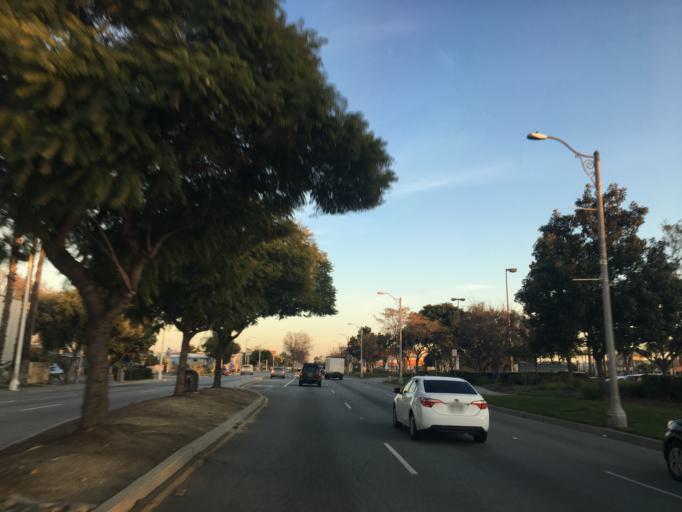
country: US
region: California
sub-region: Los Angeles County
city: Pico Rivera
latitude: 33.9871
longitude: -118.1043
